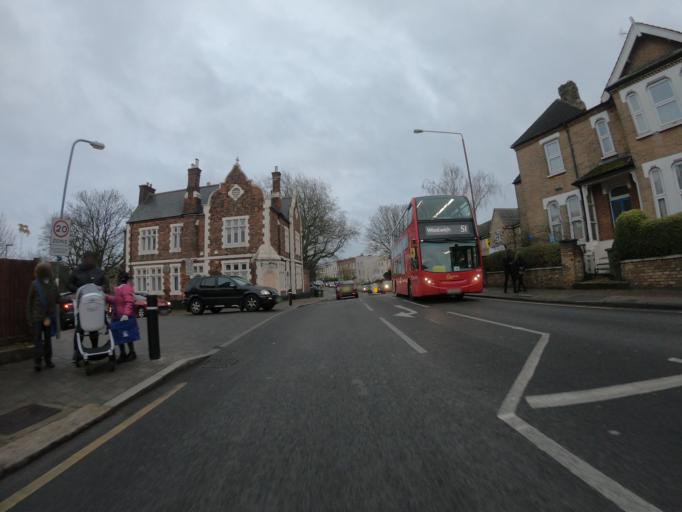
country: GB
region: England
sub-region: Greater London
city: Woolwich
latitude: 51.4819
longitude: 0.0731
